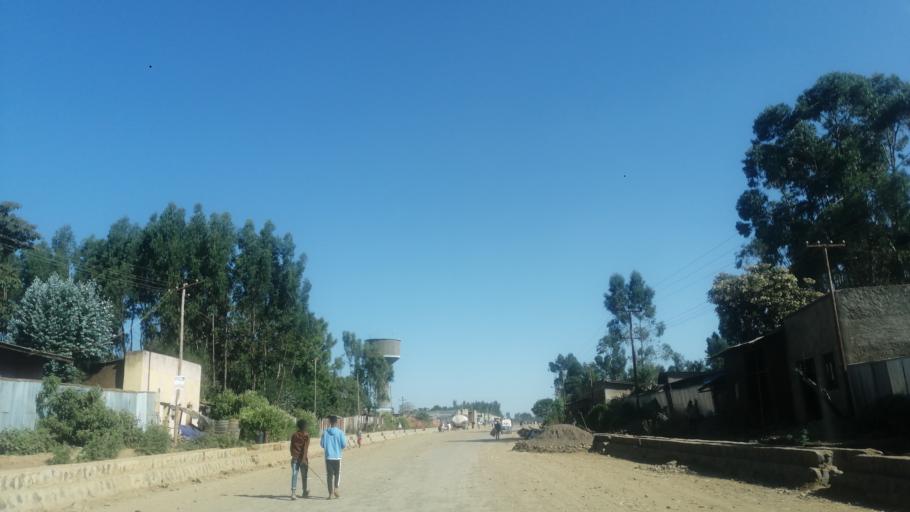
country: ET
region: Amhara
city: Addiet Canna
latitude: 11.0838
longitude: 37.8744
